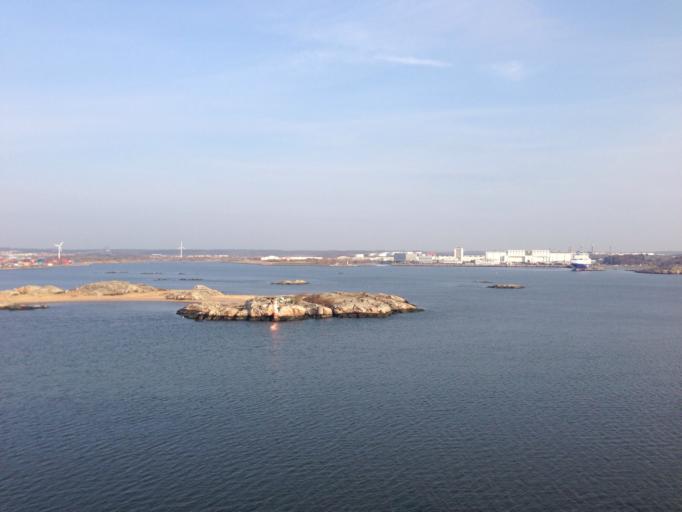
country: SE
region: Vaestra Goetaland
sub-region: Goteborg
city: Torslanda
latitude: 57.6799
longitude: 11.8203
